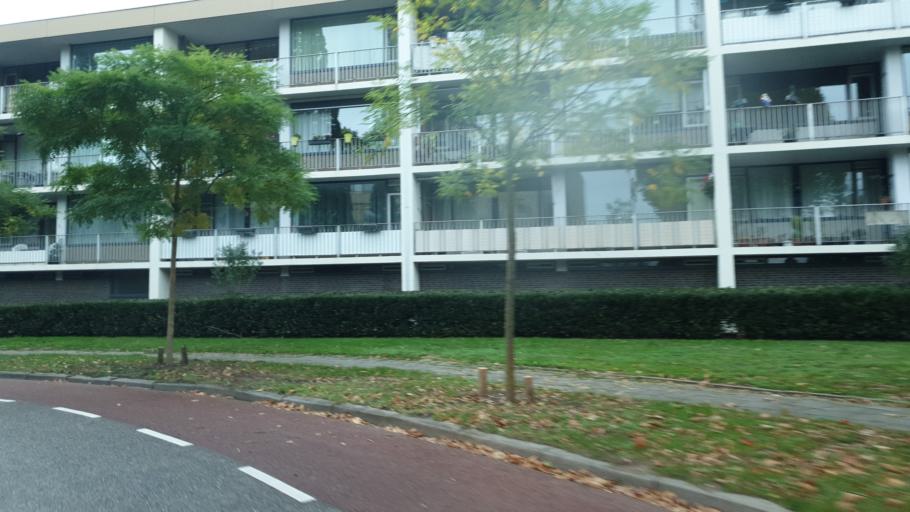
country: NL
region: Gelderland
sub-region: Gemeente Nijmegen
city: Lindenholt
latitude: 51.8158
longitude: 5.8087
